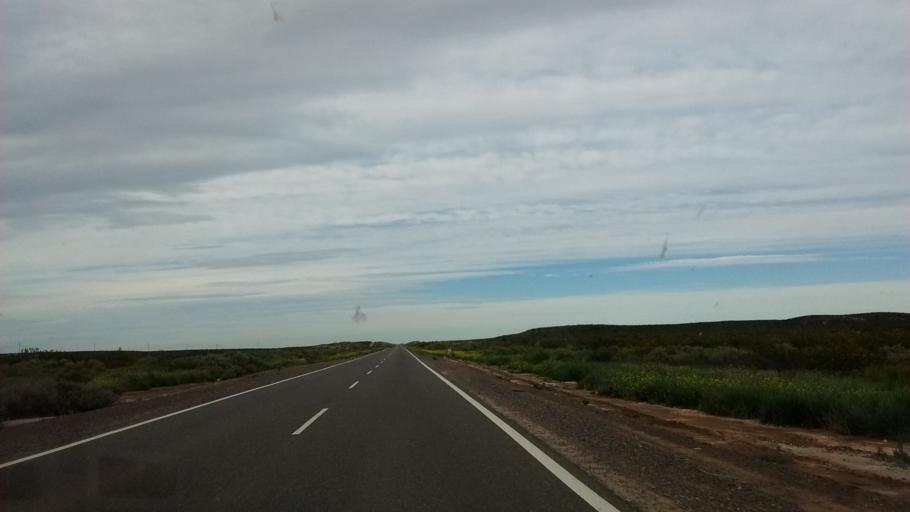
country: AR
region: Rio Negro
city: Contraalmirante Cordero
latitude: -38.4506
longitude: -68.0436
